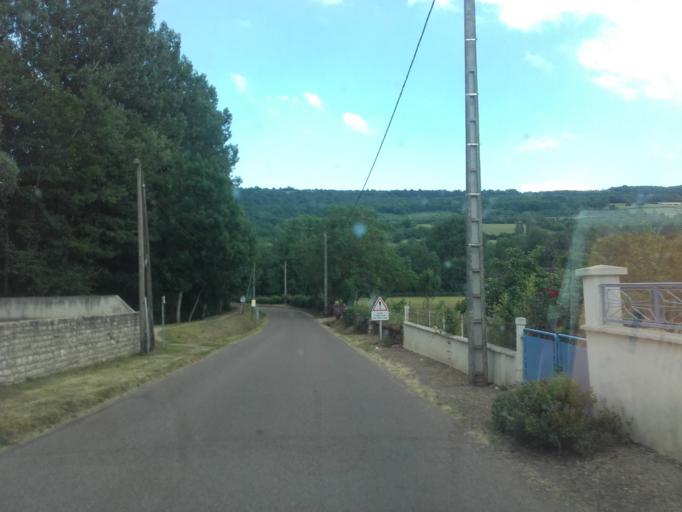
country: FR
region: Bourgogne
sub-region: Departement de Saone-et-Loire
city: Saint-Leger-sur-Dheune
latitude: 46.8925
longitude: 4.6769
